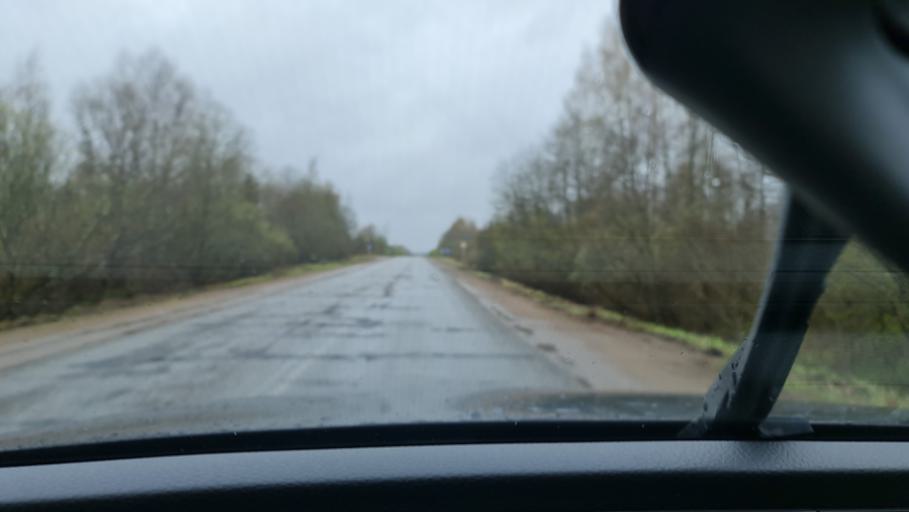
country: RU
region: Novgorod
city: Kresttsy
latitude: 58.0161
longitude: 32.7879
